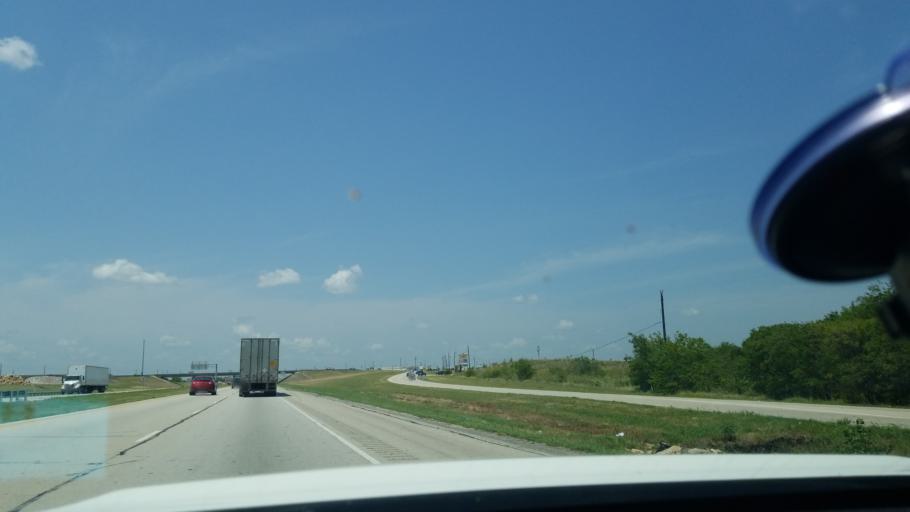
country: US
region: Texas
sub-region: Tarrant County
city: Blue Mound
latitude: 32.8959
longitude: -97.3281
